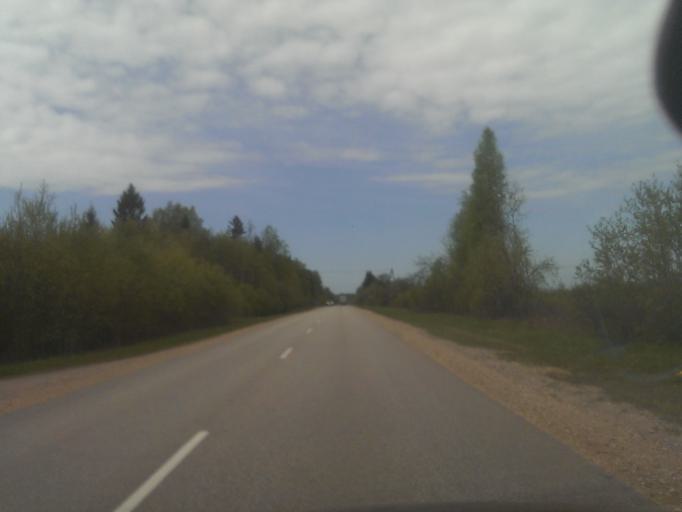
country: LV
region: Ventspils Rajons
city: Piltene
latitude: 57.1692
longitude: 21.6750
